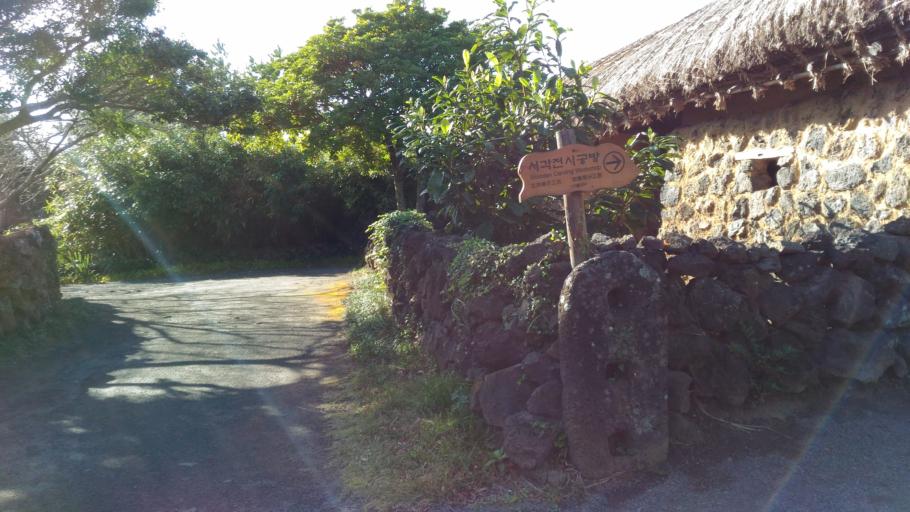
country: KR
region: Jeju-do
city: Seogwipo
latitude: 33.3222
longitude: 126.8402
